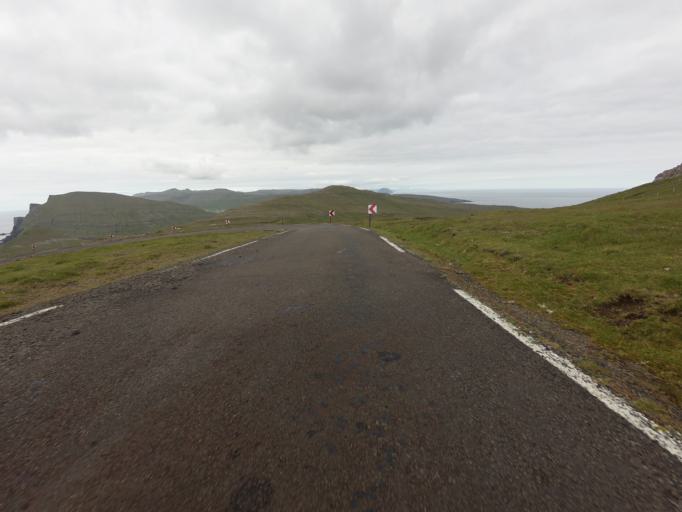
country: FO
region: Suduroy
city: Vagur
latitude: 61.4275
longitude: -6.7525
